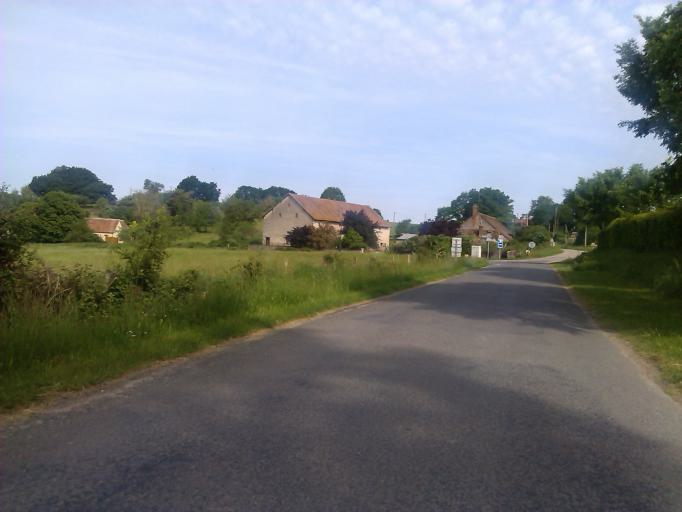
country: FR
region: Auvergne
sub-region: Departement de l'Allier
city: Vallon-en-Sully
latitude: 46.6117
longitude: 2.6582
